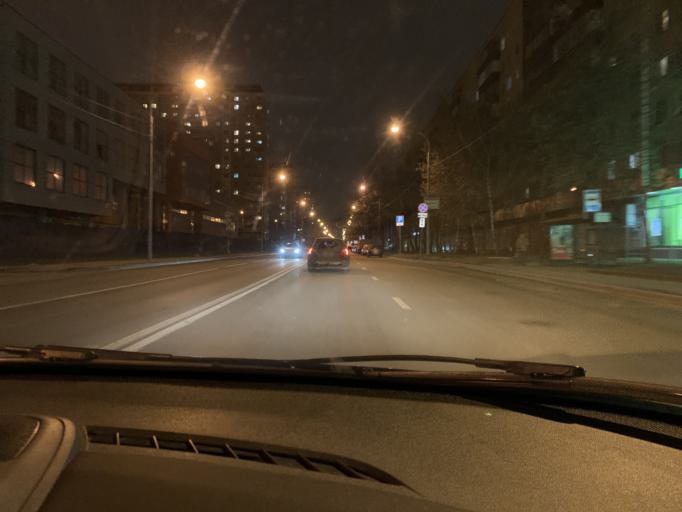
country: RU
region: Moskovskaya
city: Vostochnoe Degunino
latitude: 55.8682
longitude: 37.5629
